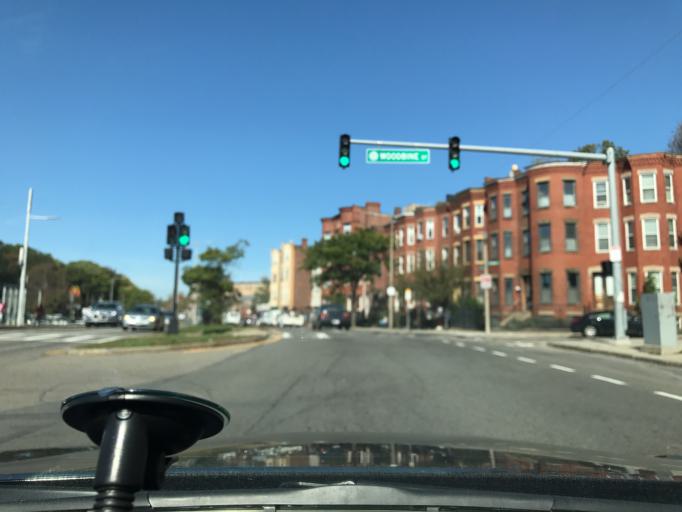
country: US
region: Massachusetts
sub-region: Suffolk County
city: South Boston
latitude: 42.3195
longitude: -71.0814
